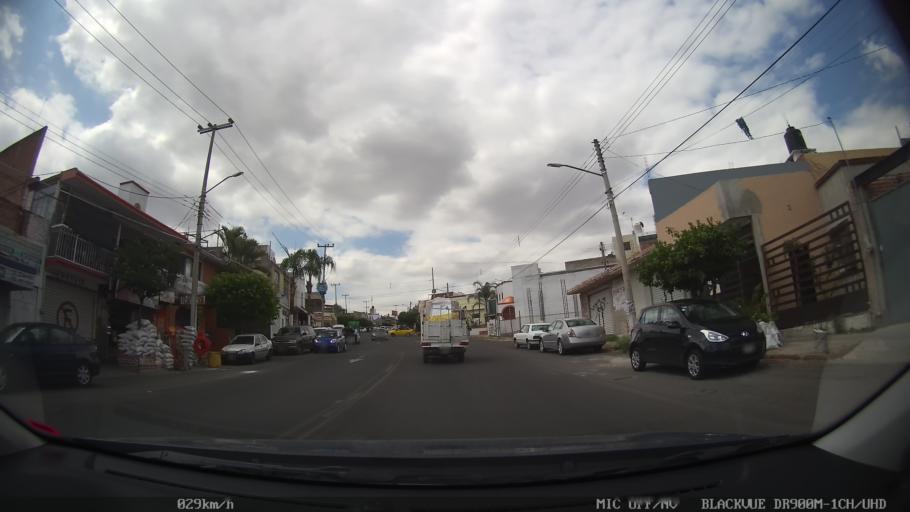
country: MX
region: Jalisco
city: Tonala
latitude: 20.6290
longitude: -103.2521
